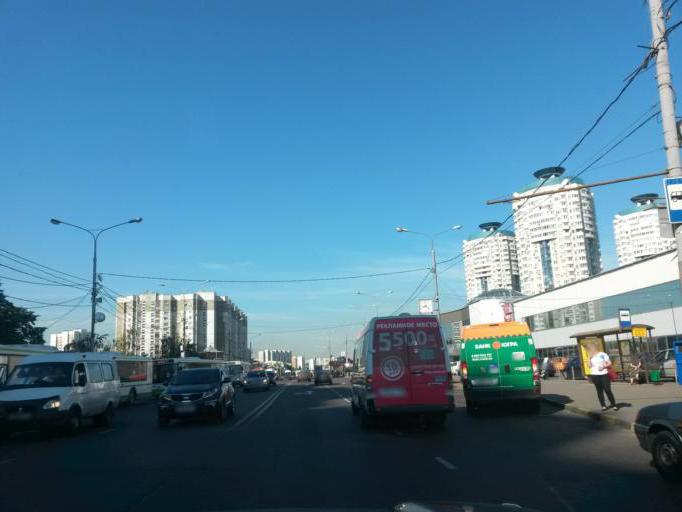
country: RU
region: Moscow
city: Lyublino
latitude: 55.6600
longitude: 37.7519
